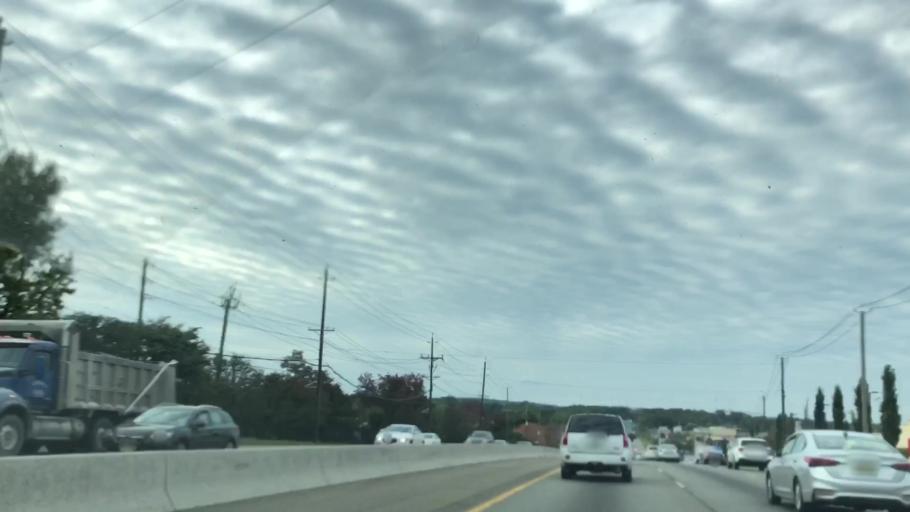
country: US
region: New Jersey
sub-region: Essex County
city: Nutley
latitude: 40.8352
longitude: -74.1500
